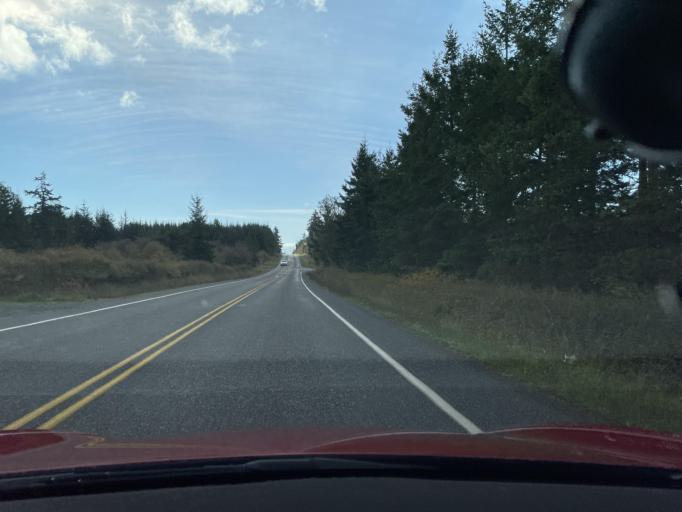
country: US
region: Washington
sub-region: San Juan County
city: Friday Harbor
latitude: 48.4830
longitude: -123.0318
